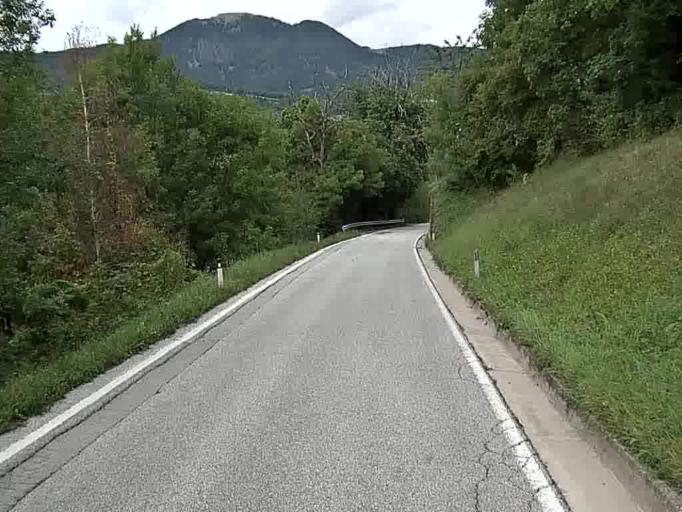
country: IT
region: Trentino-Alto Adige
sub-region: Provincia di Trento
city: Frassilongo
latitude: 46.0824
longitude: 11.2911
